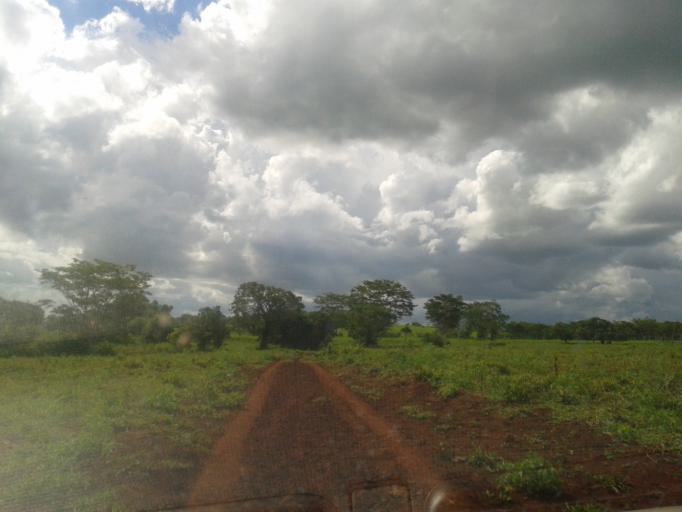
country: BR
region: Minas Gerais
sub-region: Capinopolis
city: Capinopolis
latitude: -18.7721
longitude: -49.8280
